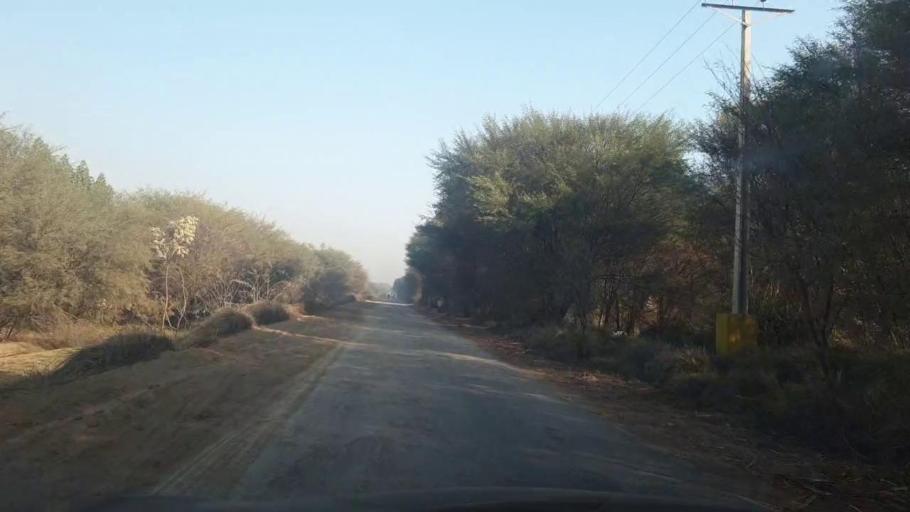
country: PK
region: Sindh
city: Mirpur Mathelo
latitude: 28.0503
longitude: 69.4607
